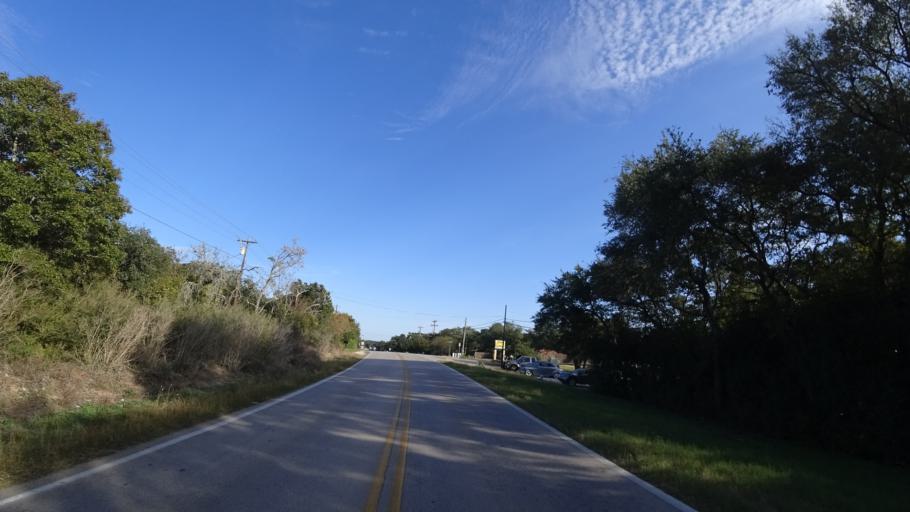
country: US
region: Texas
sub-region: Travis County
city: Barton Creek
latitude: 30.2361
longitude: -97.9143
